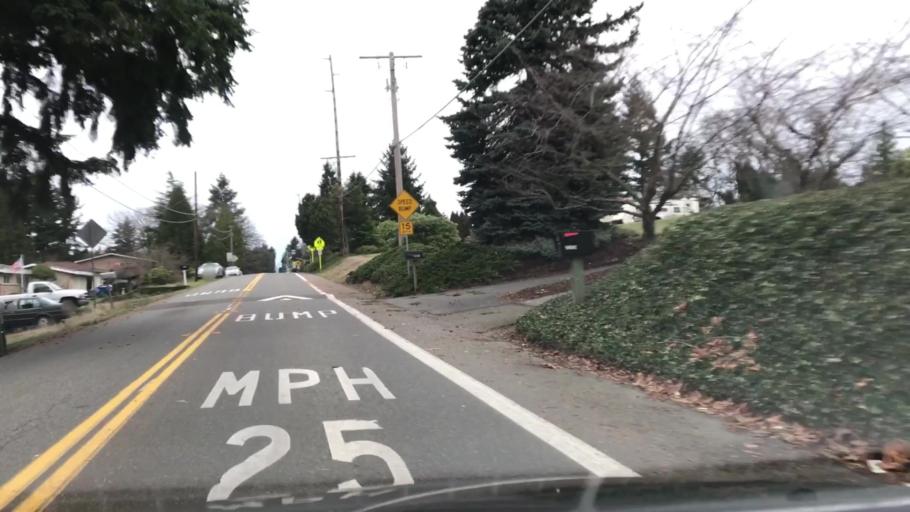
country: US
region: Washington
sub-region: King County
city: East Hill-Meridian
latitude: 47.4092
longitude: -122.2075
